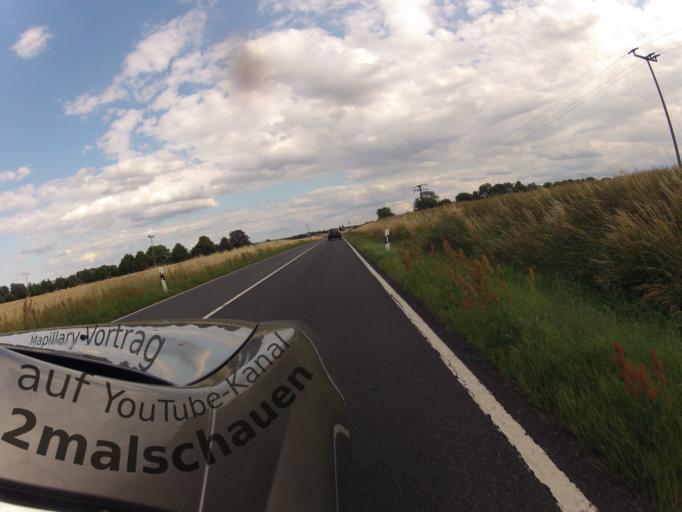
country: DE
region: Mecklenburg-Vorpommern
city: Seebad Bansin
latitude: 53.8957
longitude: 14.0672
